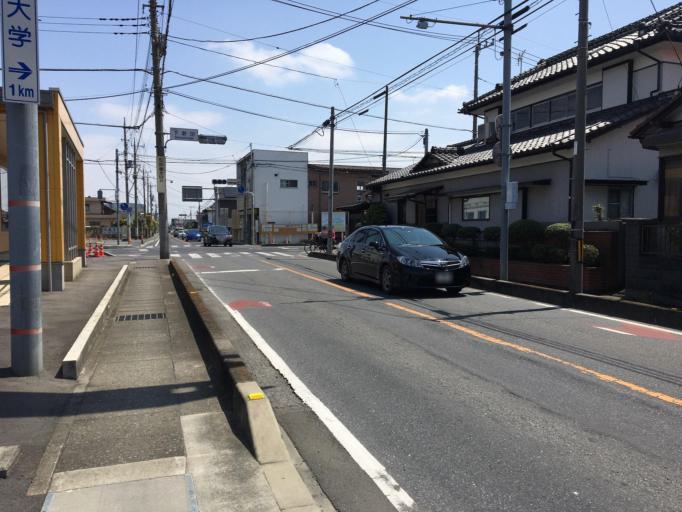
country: JP
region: Gunma
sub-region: Sawa-gun
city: Tamamura
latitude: 36.3030
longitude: 139.1162
